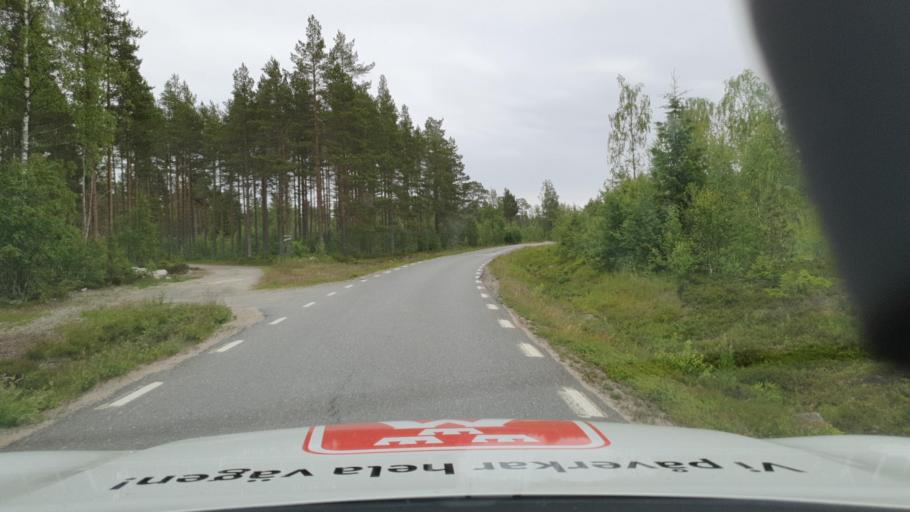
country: SE
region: Vaesterbotten
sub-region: Nordmalings Kommun
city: Nordmaling
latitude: 63.4313
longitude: 19.4901
